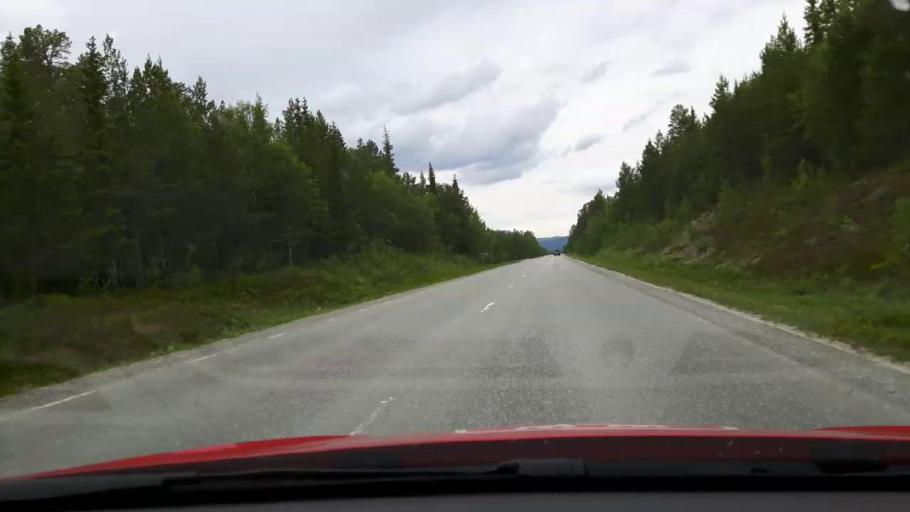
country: NO
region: Hedmark
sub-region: Engerdal
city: Engerdal
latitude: 62.5275
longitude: 12.5770
